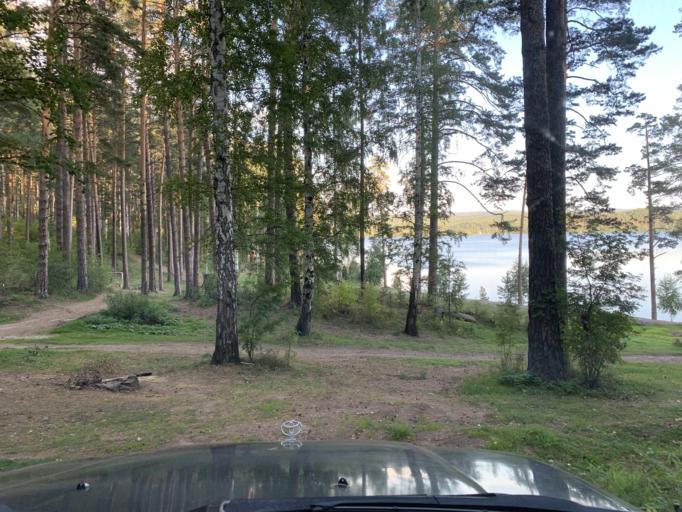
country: RU
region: Chelyabinsk
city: Vishnevogorsk
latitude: 55.9979
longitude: 60.5060
